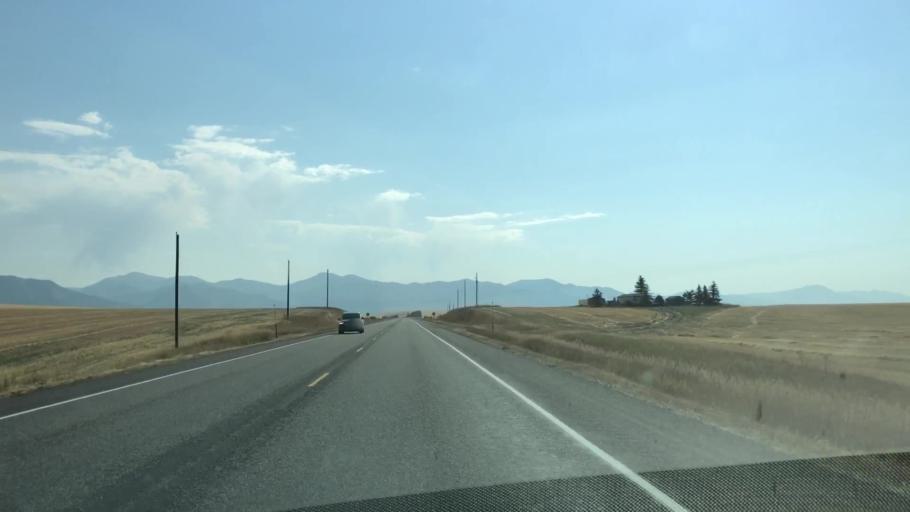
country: US
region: Idaho
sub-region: Madison County
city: Rexburg
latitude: 43.5861
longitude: -111.5946
